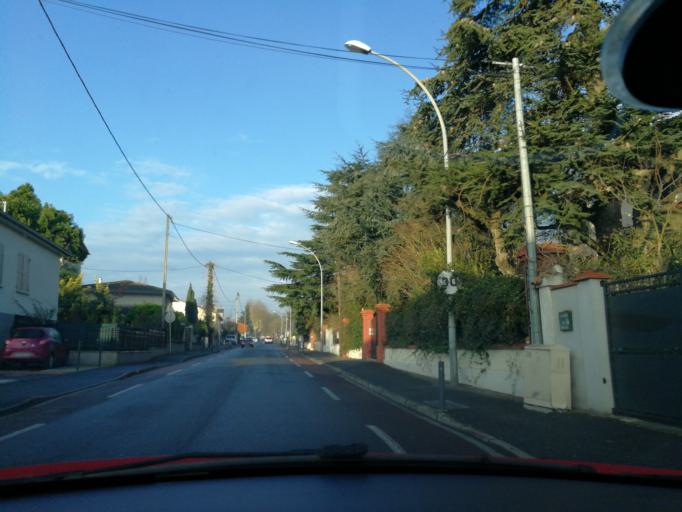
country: FR
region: Midi-Pyrenees
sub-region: Departement de la Haute-Garonne
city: Blagnac
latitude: 43.6258
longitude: 1.3958
